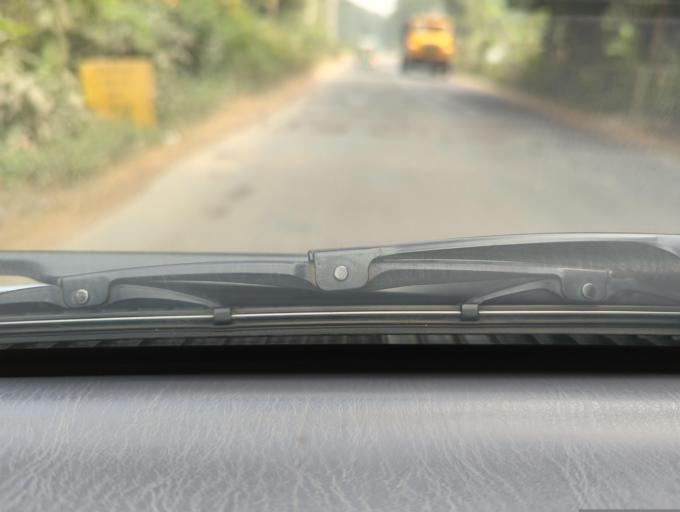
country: BD
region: Sylhet
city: Maulavi Bazar
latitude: 24.4974
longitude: 91.7400
